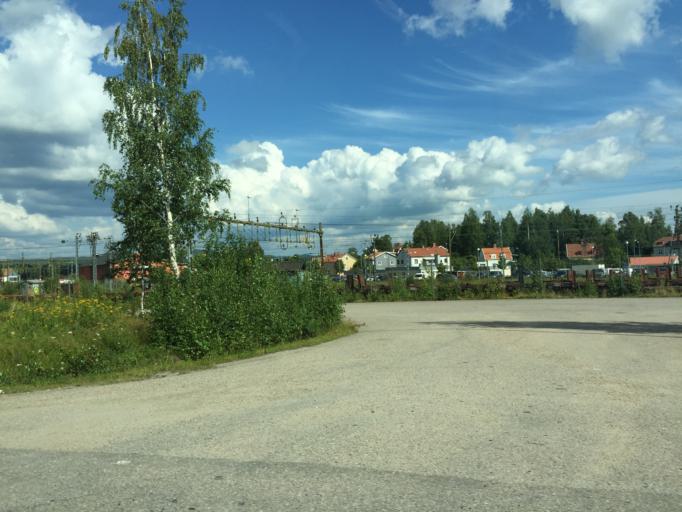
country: SE
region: Gaevleborg
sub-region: Bollnas Kommun
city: Bollnas
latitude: 61.3519
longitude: 16.3914
